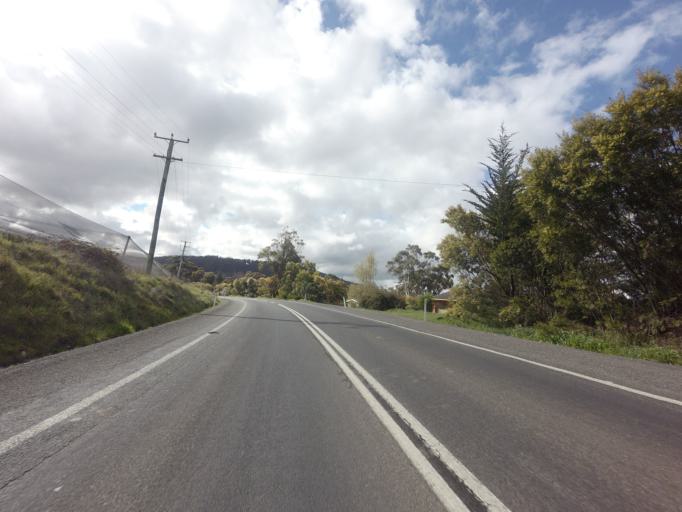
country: AU
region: Tasmania
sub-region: Huon Valley
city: Geeveston
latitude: -43.1459
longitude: 146.9781
